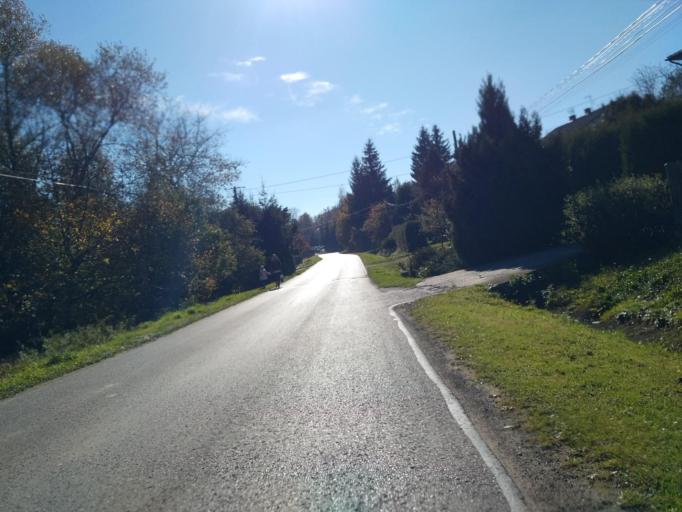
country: PL
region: Subcarpathian Voivodeship
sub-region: Powiat ropczycko-sedziszowski
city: Iwierzyce
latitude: 49.9880
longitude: 21.7265
